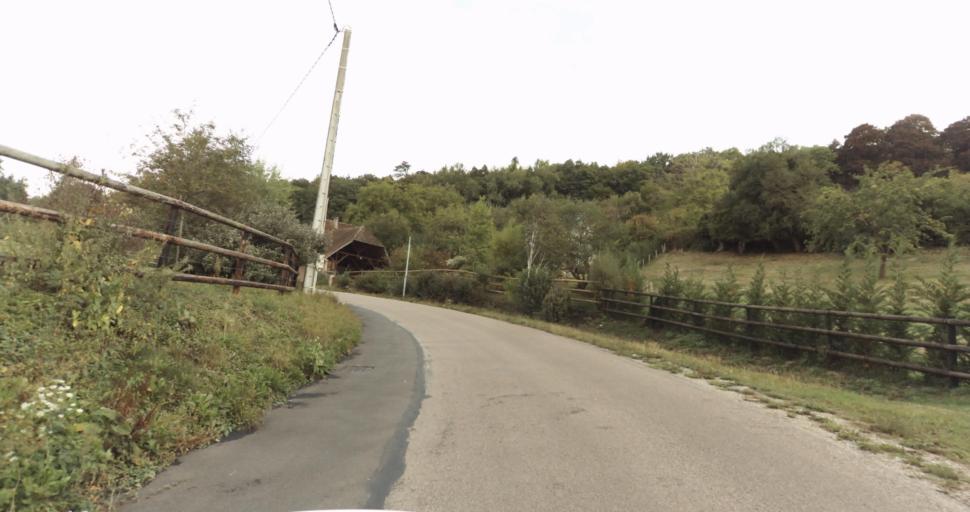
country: FR
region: Lower Normandy
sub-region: Departement de l'Orne
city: Vimoutiers
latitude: 48.9267
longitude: 0.1871
